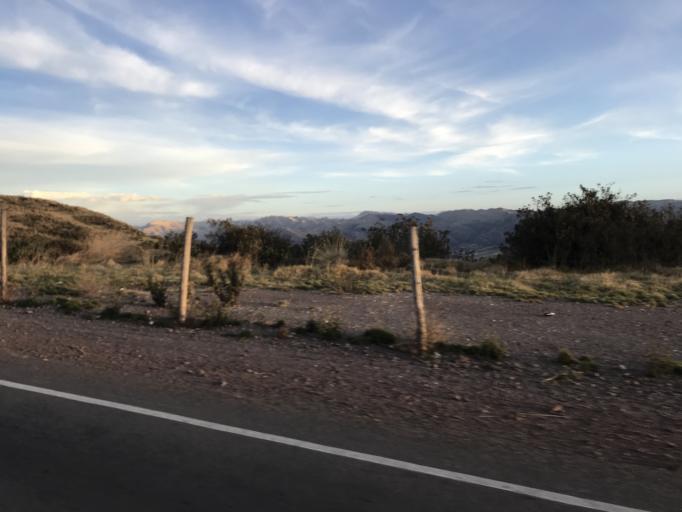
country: PE
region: Cusco
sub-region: Provincia de Cusco
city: Cusco
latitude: -13.4944
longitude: -71.9691
